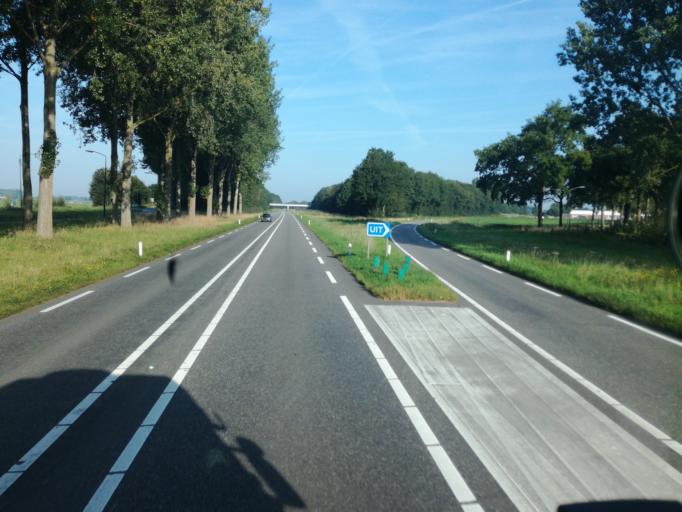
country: NL
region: North Brabant
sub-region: Gemeente Heusden
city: Heusden
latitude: 51.7203
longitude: 5.1351
